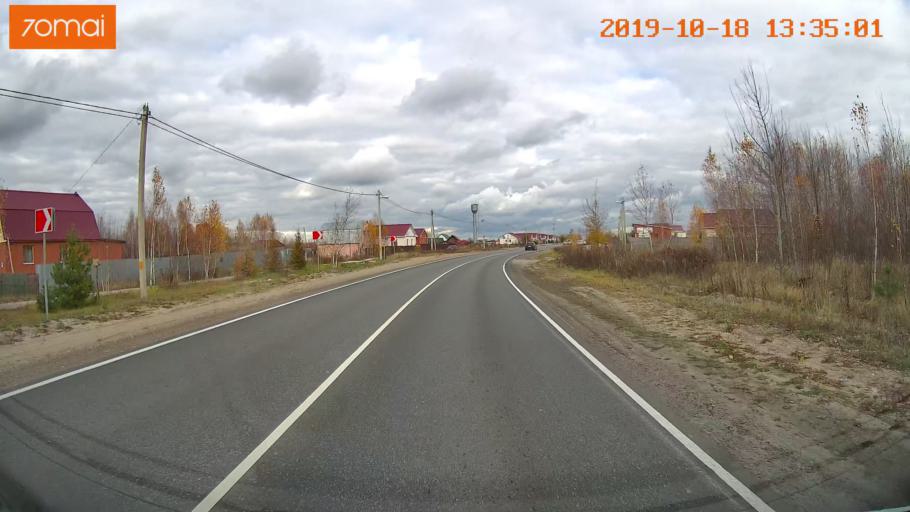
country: RU
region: Rjazan
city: Solotcha
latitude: 54.8585
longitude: 39.9621
